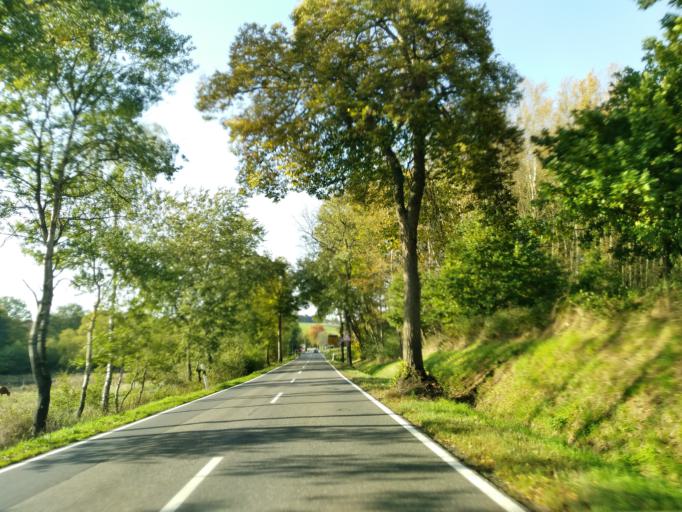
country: DE
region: Rheinland-Pfalz
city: Asbach
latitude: 50.6645
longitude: 7.3986
